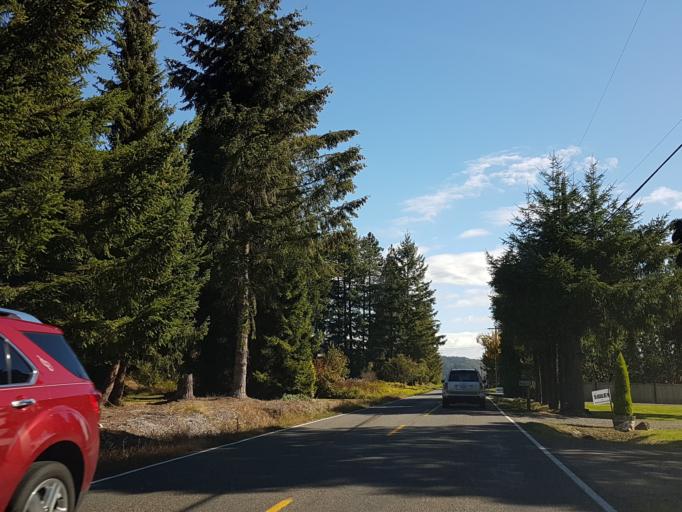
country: US
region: Washington
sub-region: Snohomish County
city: Cathcart
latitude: 47.8484
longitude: -122.1097
